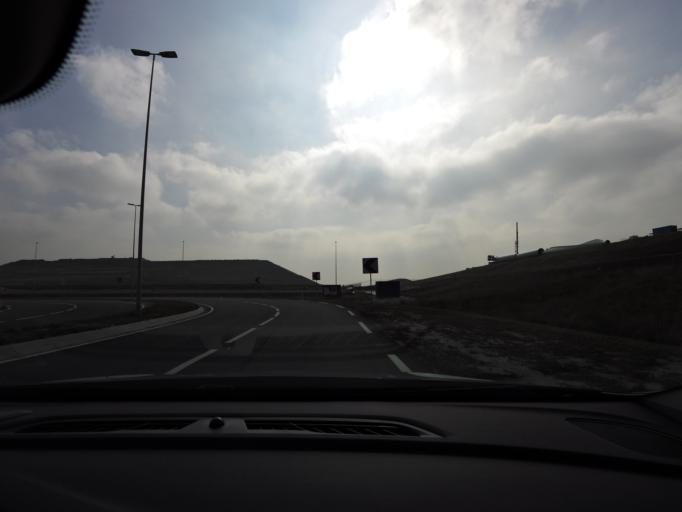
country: NL
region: South Holland
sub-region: Gemeente Goeree-Overflakkee
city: Goedereede
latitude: 51.9287
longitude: 4.0185
